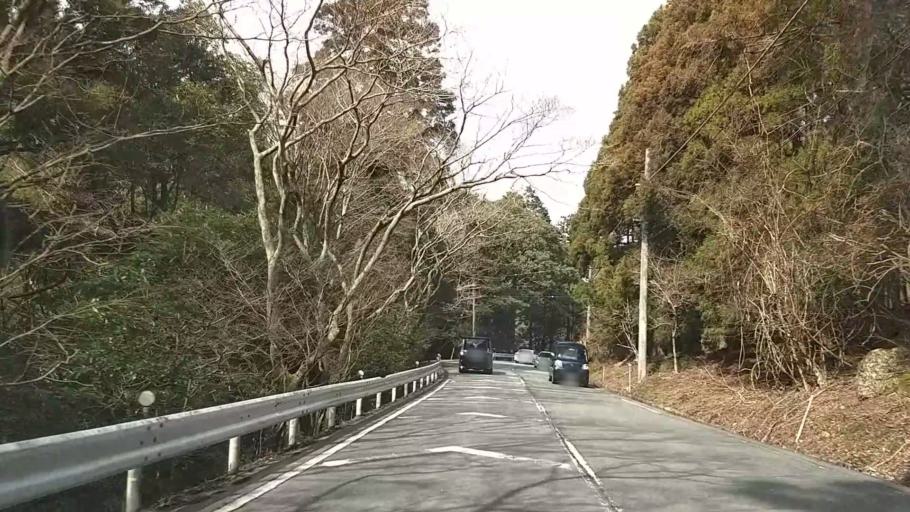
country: JP
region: Shizuoka
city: Shimoda
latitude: 34.8444
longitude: 138.9220
